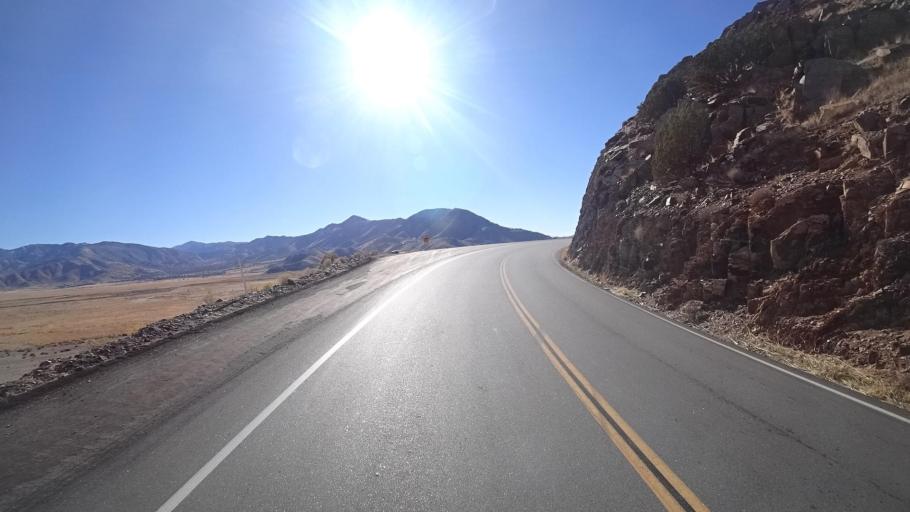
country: US
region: California
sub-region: Kern County
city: Wofford Heights
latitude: 35.6772
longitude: -118.4144
